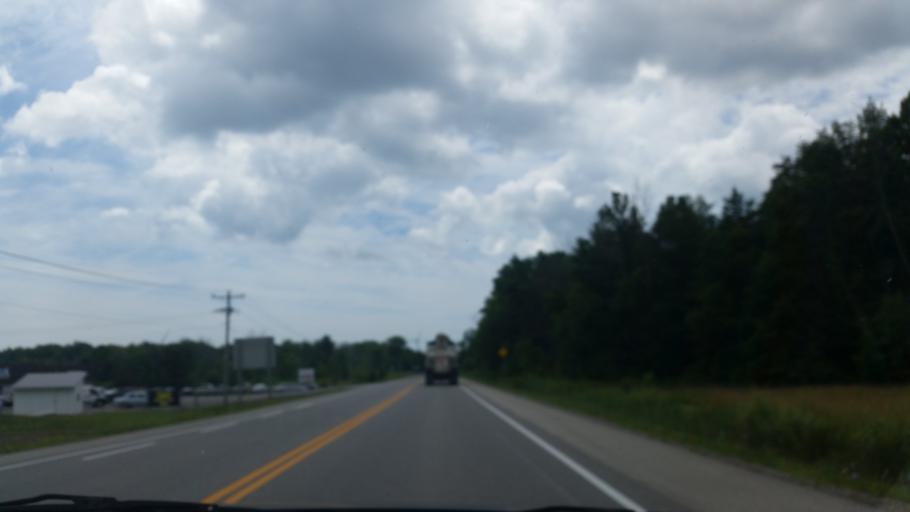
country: CA
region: Ontario
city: Norfolk County
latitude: 42.8201
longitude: -80.1501
